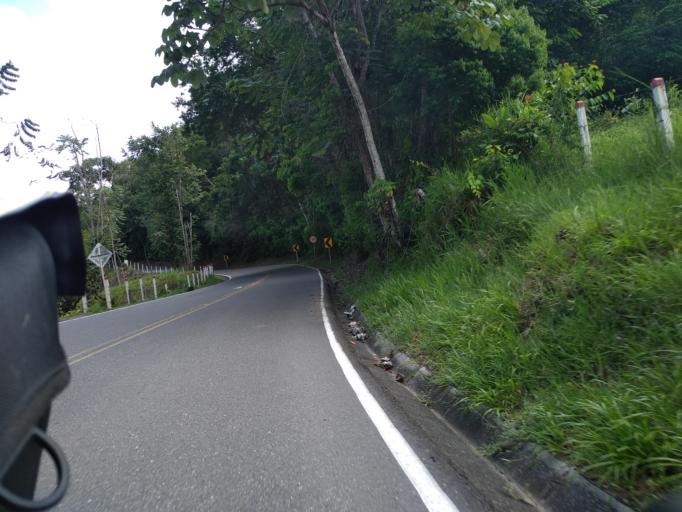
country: CO
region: Santander
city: Cimitarra
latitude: 6.4356
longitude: -74.0150
